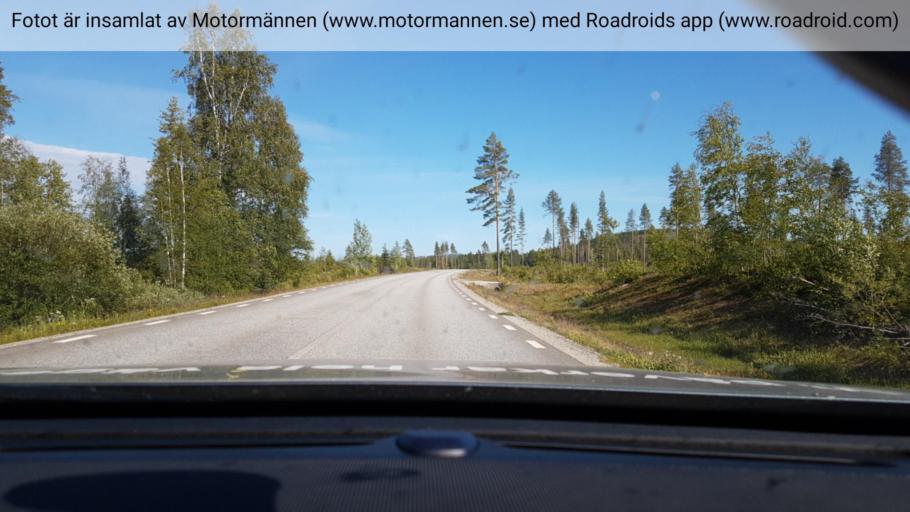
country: SE
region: Vaesterbotten
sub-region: Lycksele Kommun
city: Lycksele
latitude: 64.6446
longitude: 18.5033
